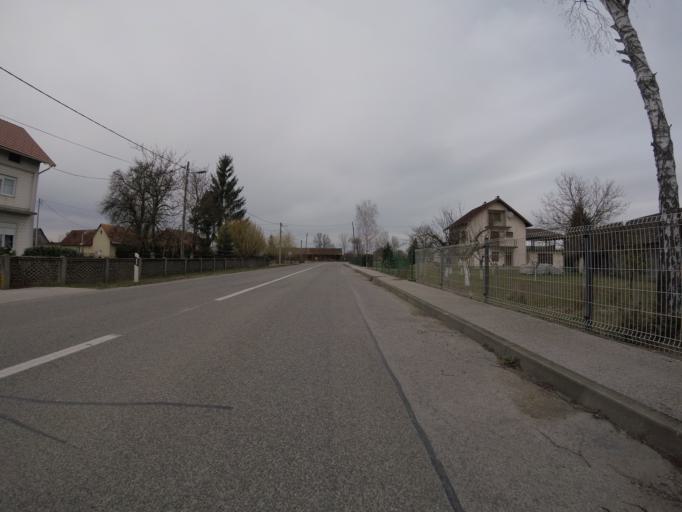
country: HR
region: Grad Zagreb
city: Horvati
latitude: 45.5744
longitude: 15.8611
